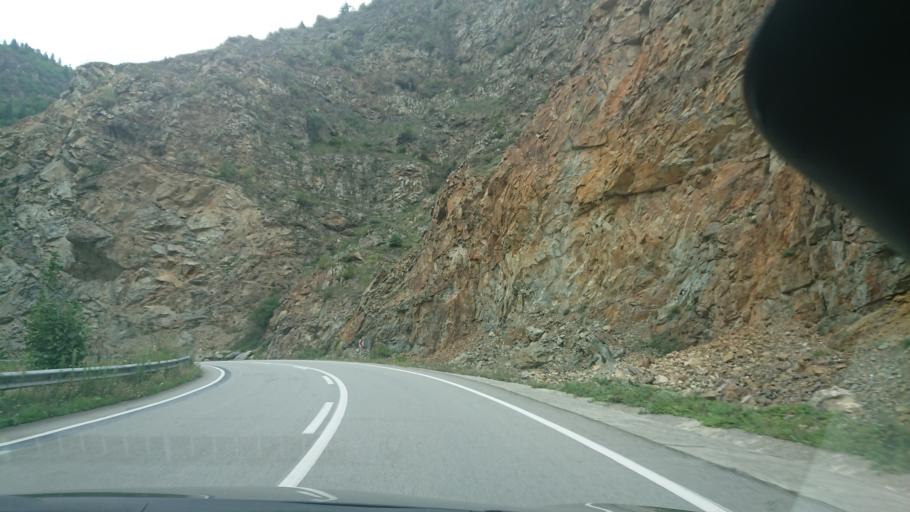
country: TR
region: Gumushane
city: Kurtun
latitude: 40.7352
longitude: 39.0070
